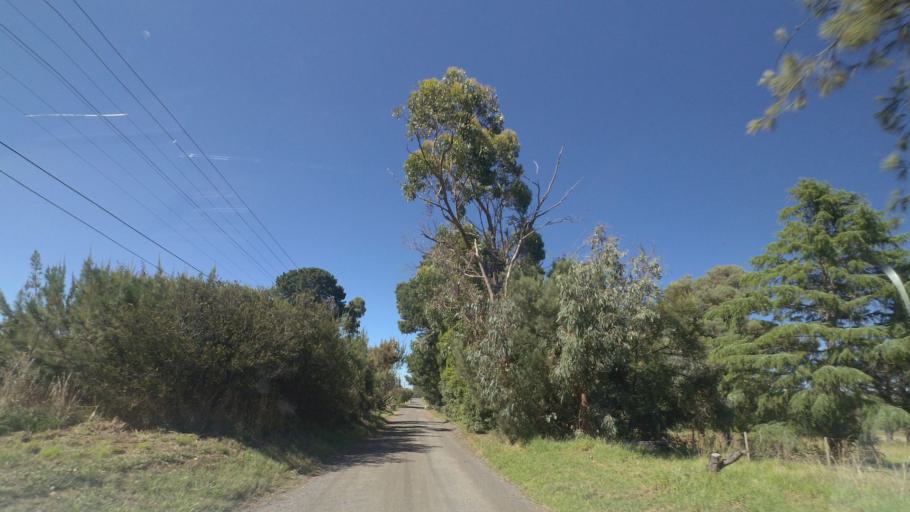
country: AU
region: Victoria
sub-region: Knox
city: Wantirna South
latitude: -37.8724
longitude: 145.1999
